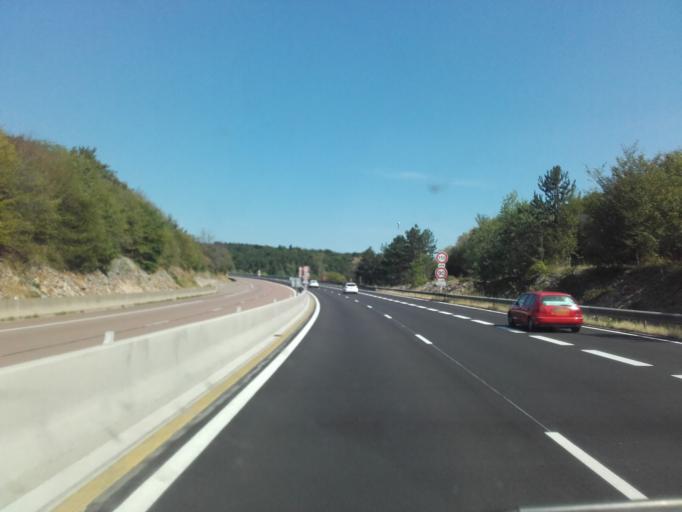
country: FR
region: Bourgogne
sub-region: Departement de la Cote-d'Or
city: Savigny-les-Beaune
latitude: 47.1010
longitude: 4.7220
